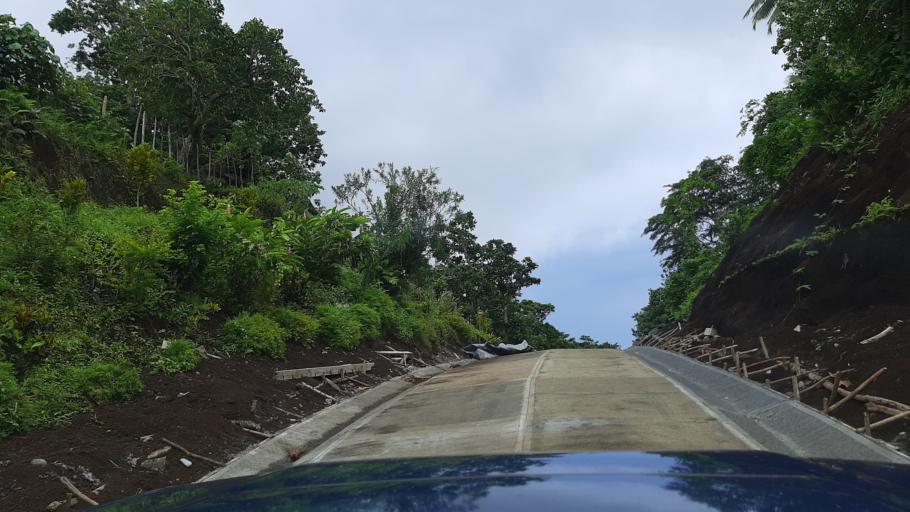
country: VU
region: Shefa
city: Port-Vila
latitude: -16.9006
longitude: 168.5735
